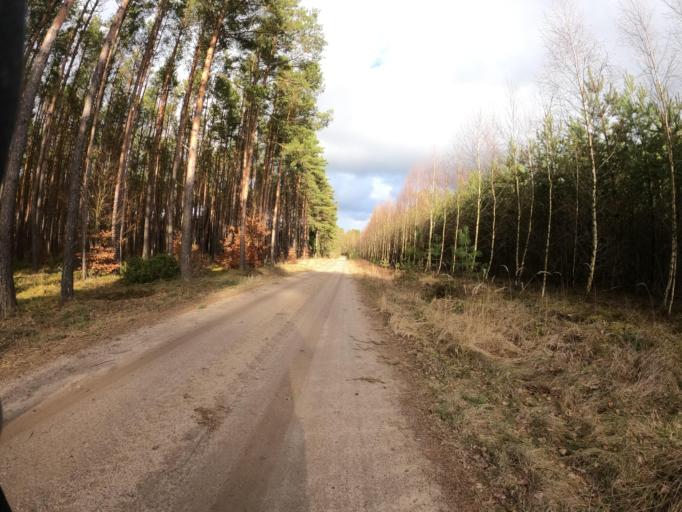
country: PL
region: Greater Poland Voivodeship
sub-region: Powiat zlotowski
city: Sypniewo
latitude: 53.4329
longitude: 16.5564
